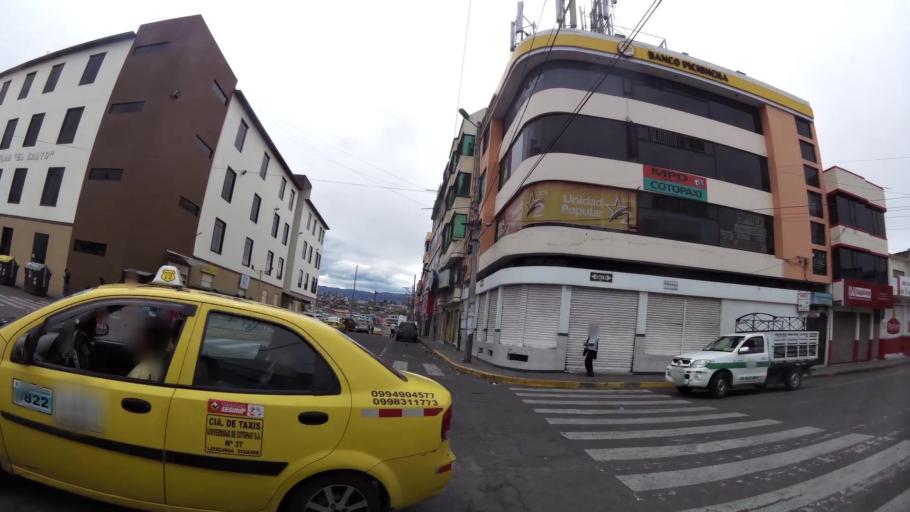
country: EC
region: Cotopaxi
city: Latacunga
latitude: -0.9307
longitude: -78.6188
